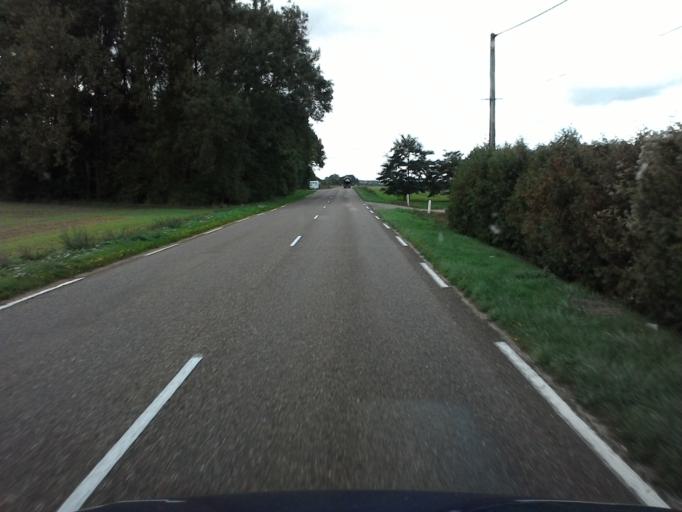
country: FR
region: Lorraine
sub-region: Departement des Vosges
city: Liffol-le-Grand
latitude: 48.3091
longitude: 5.5648
